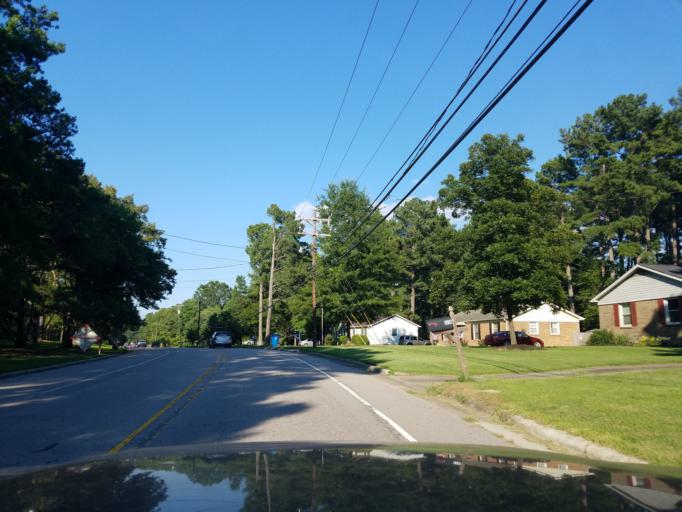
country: US
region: North Carolina
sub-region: Wake County
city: Green Level
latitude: 35.8826
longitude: -78.9108
